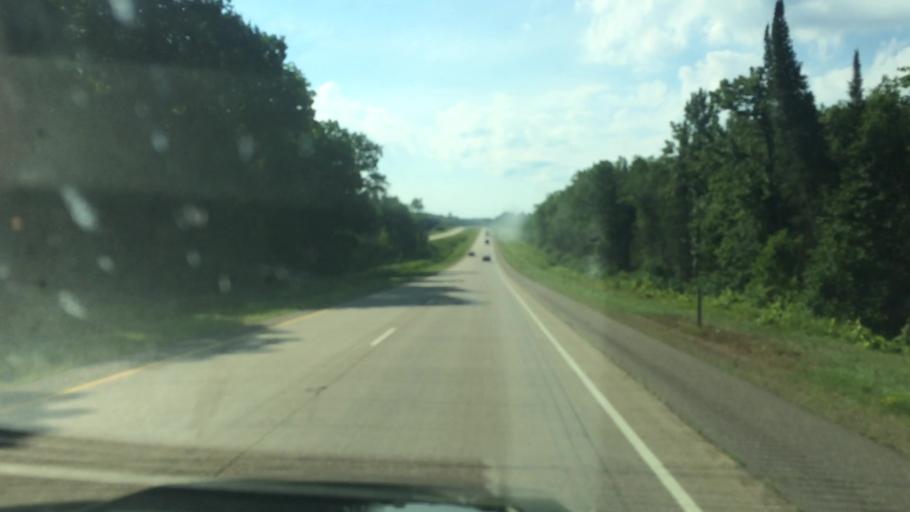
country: US
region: Wisconsin
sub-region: Shawano County
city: Wittenberg
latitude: 44.8169
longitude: -89.0506
